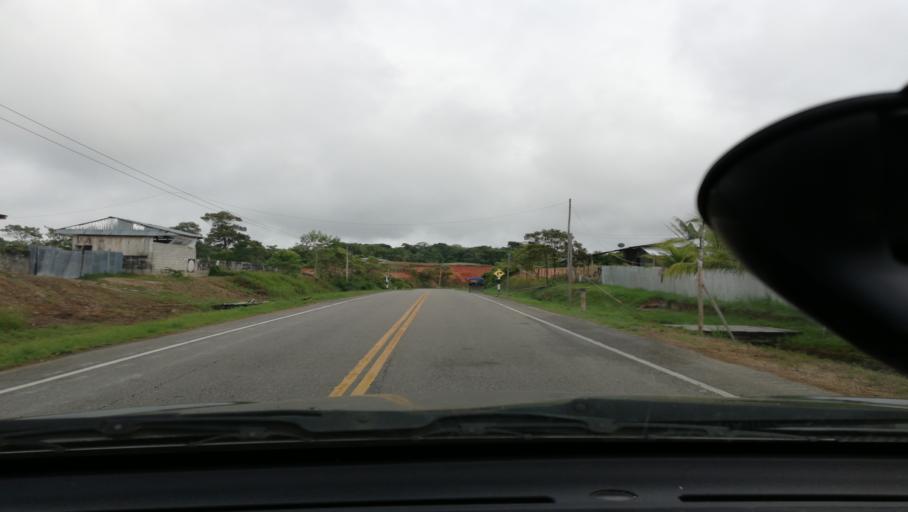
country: PE
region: Loreto
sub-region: Provincia de Loreto
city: Nauta
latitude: -4.4980
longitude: -73.5919
